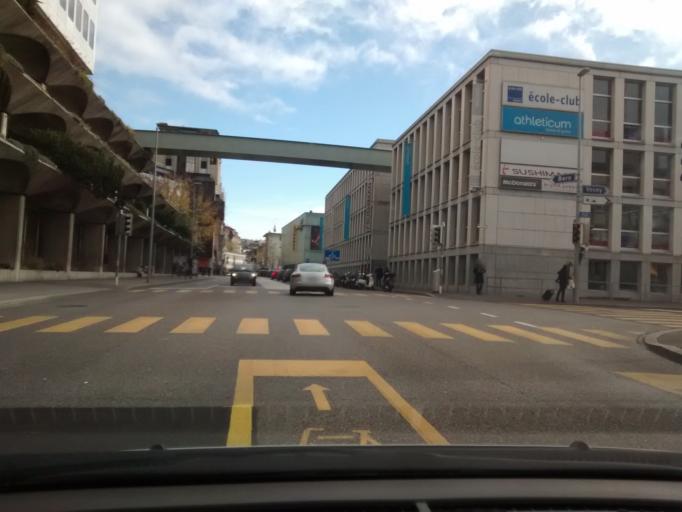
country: CH
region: Vaud
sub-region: Lausanne District
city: Lausanne
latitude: 46.5228
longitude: 6.6248
